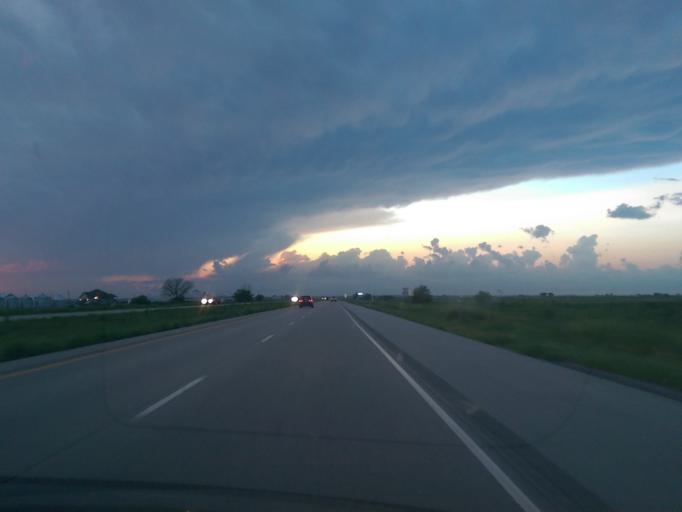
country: US
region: Nebraska
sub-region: Otoe County
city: Nebraska City
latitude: 40.6953
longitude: -95.7872
